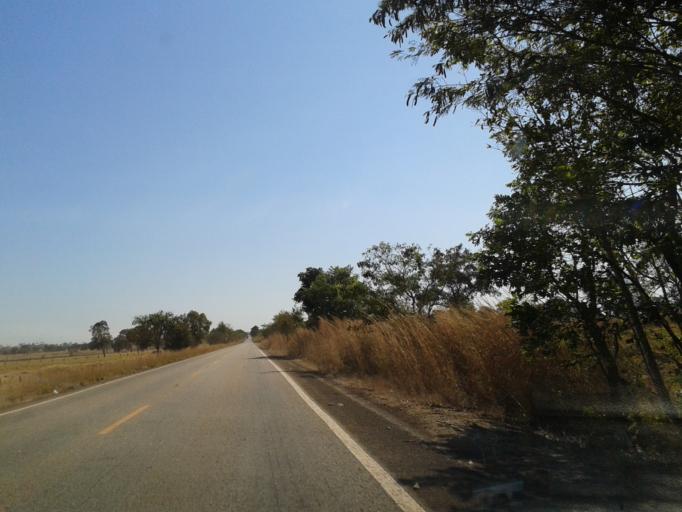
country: BR
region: Goias
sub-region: Mozarlandia
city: Mozarlandia
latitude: -14.2973
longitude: -50.4033
